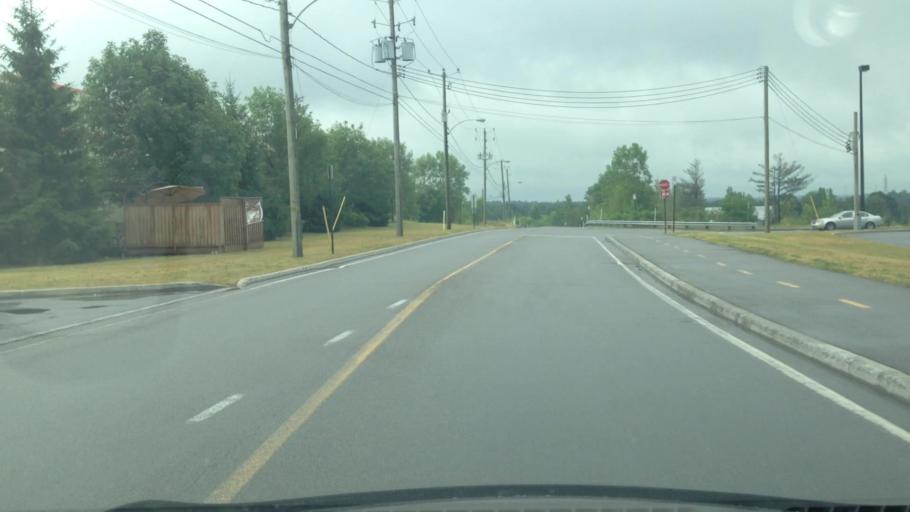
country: CA
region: Quebec
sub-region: Laurentides
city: Saint-Jerome
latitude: 45.7585
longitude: -74.0172
